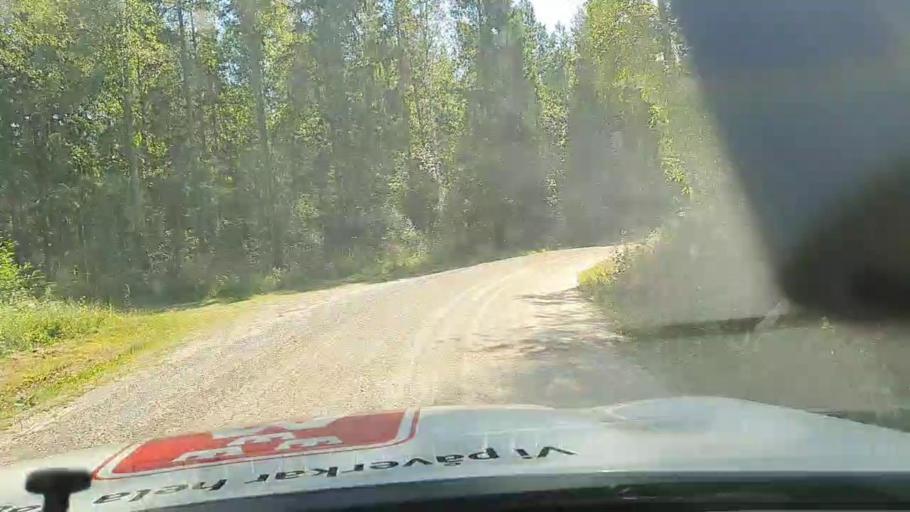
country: SE
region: Soedermanland
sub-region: Strangnas Kommun
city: Akers Styckebruk
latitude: 59.2078
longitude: 16.9186
